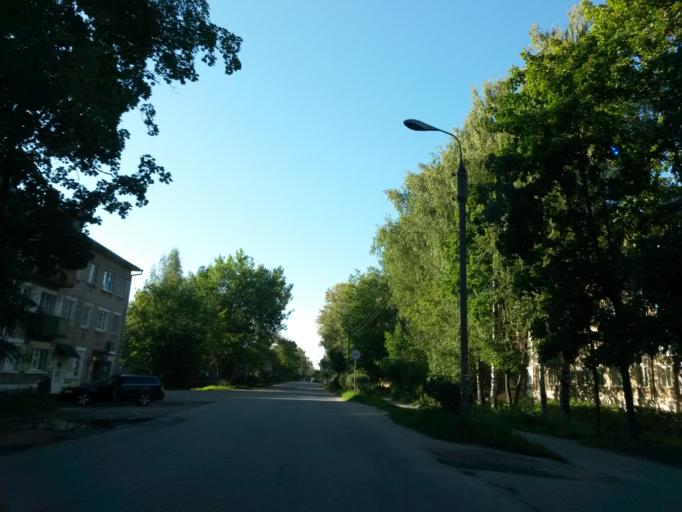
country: RU
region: Jaroslavl
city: Gavrilov-Yam
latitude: 57.3013
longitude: 39.8635
